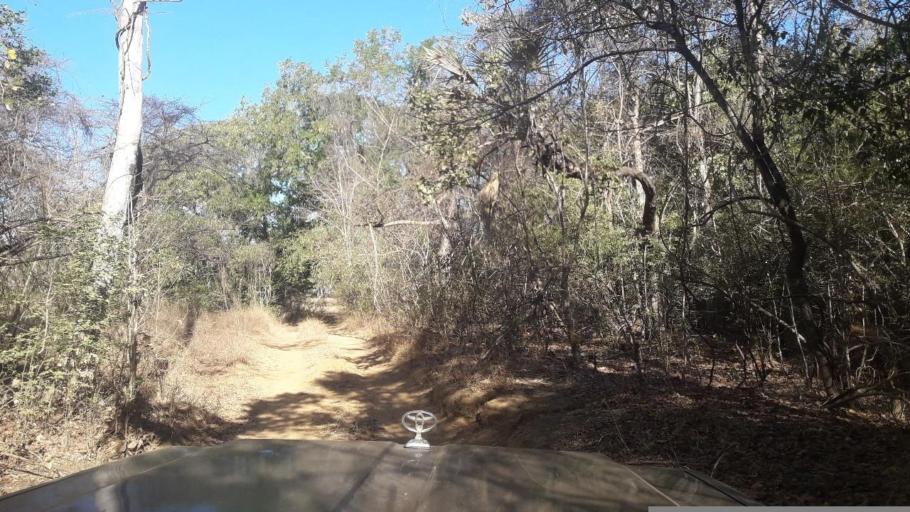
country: MG
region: Boeny
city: Sitampiky
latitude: -16.3967
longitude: 45.5950
